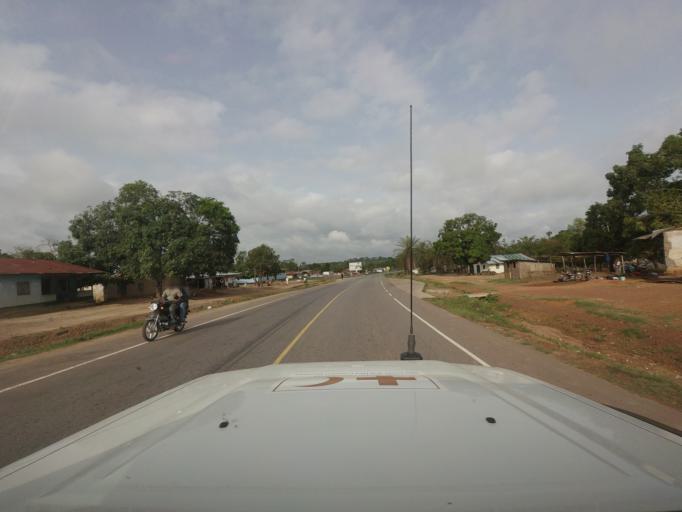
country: LR
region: Bong
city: Gbarnga
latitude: 7.0018
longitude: -9.2886
